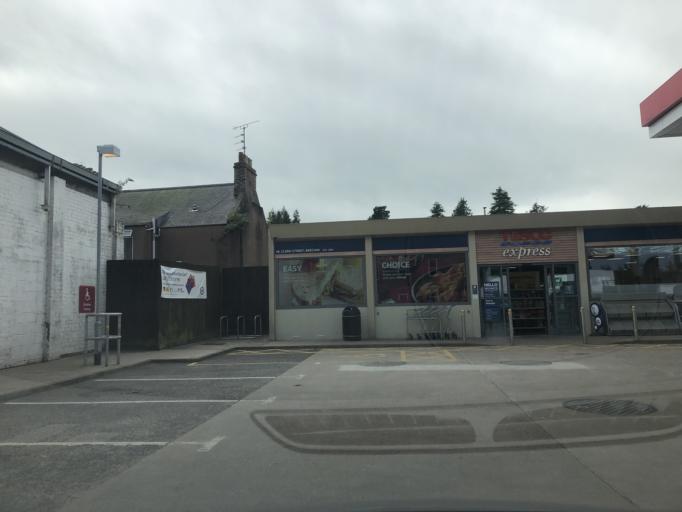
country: GB
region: Scotland
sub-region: Angus
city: Brechin
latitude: 56.7342
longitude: -2.6599
